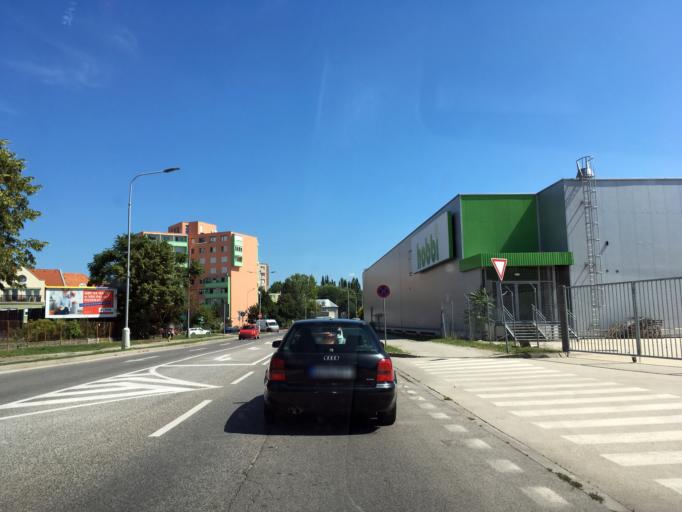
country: SK
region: Nitriansky
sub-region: Okres Nove Zamky
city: Nove Zamky
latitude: 47.9837
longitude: 18.1719
